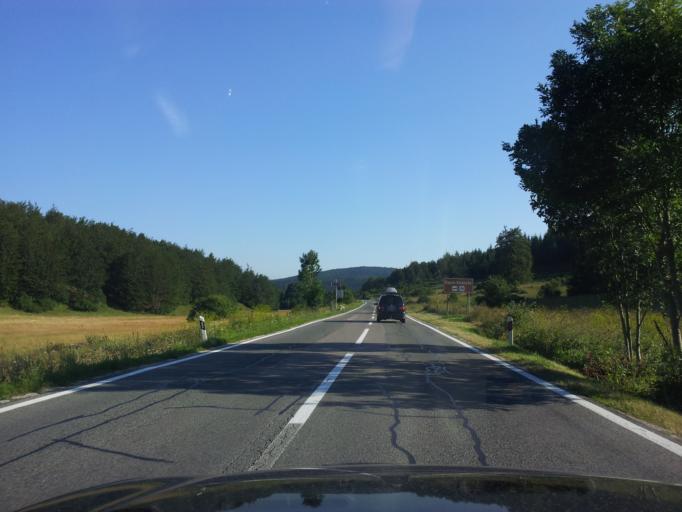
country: HR
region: Licko-Senjska
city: Jezerce
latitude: 44.8029
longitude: 15.6832
